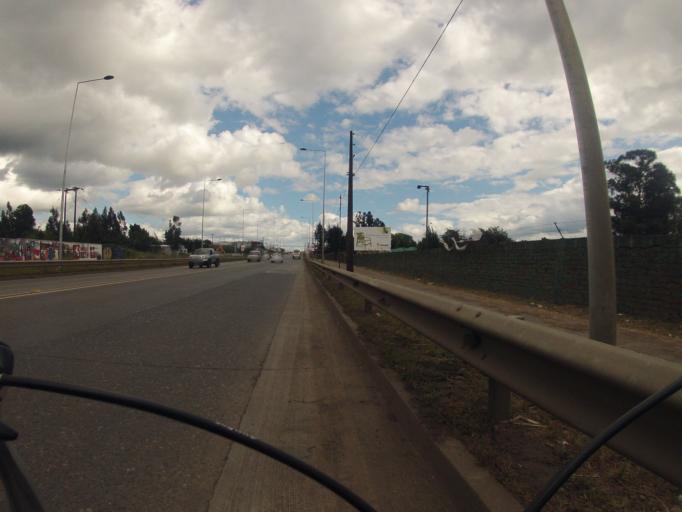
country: CL
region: Araucania
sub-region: Provincia de Cautin
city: Temuco
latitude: -38.7593
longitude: -72.6094
